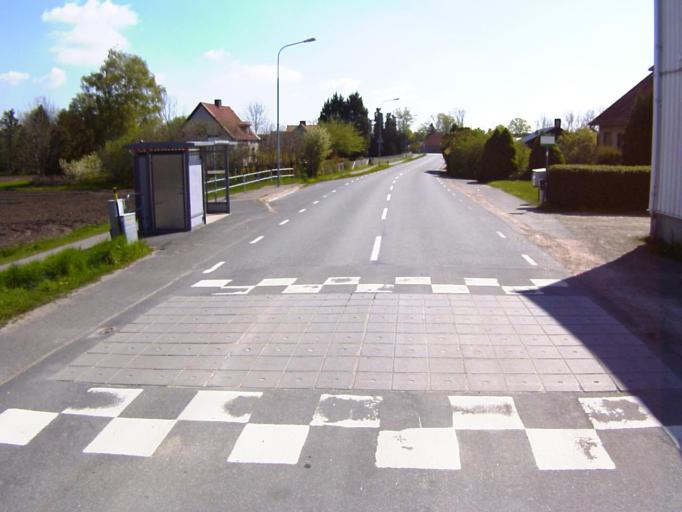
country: SE
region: Skane
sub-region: Kristianstads Kommun
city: Fjalkinge
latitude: 56.0111
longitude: 14.2358
